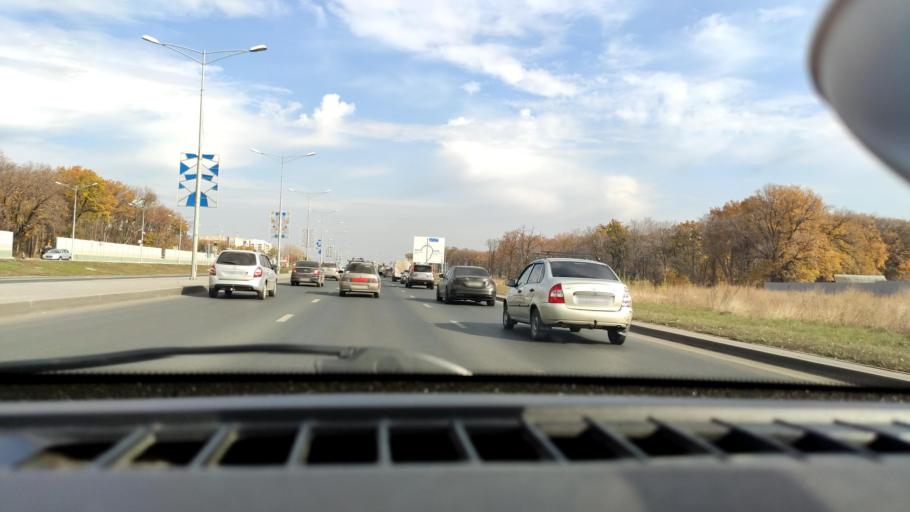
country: RU
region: Samara
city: Petra-Dubrava
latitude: 53.2711
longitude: 50.2604
